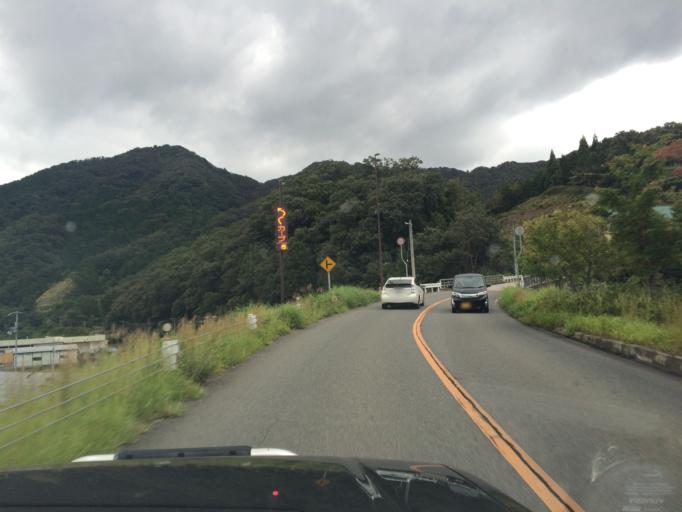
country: JP
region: Hyogo
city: Toyooka
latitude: 35.4387
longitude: 134.7946
